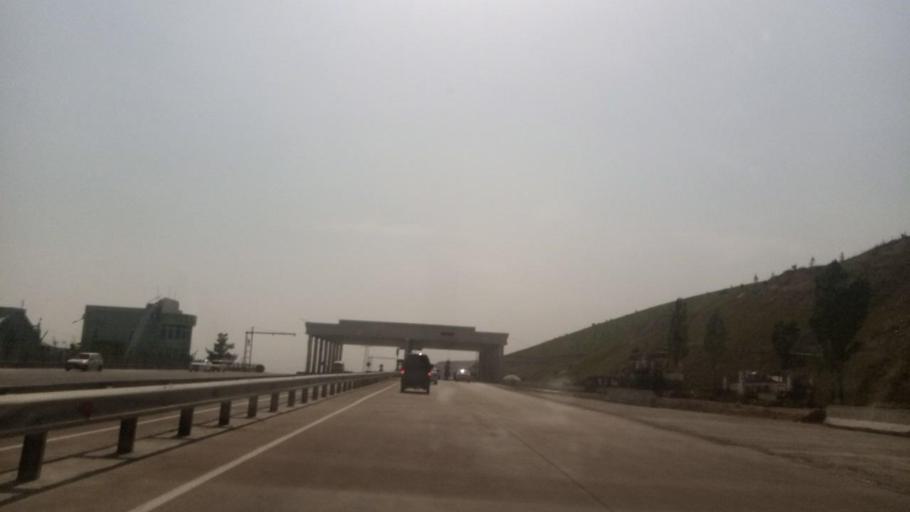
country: UZ
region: Toshkent
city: Angren
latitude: 41.0648
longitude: 70.2164
